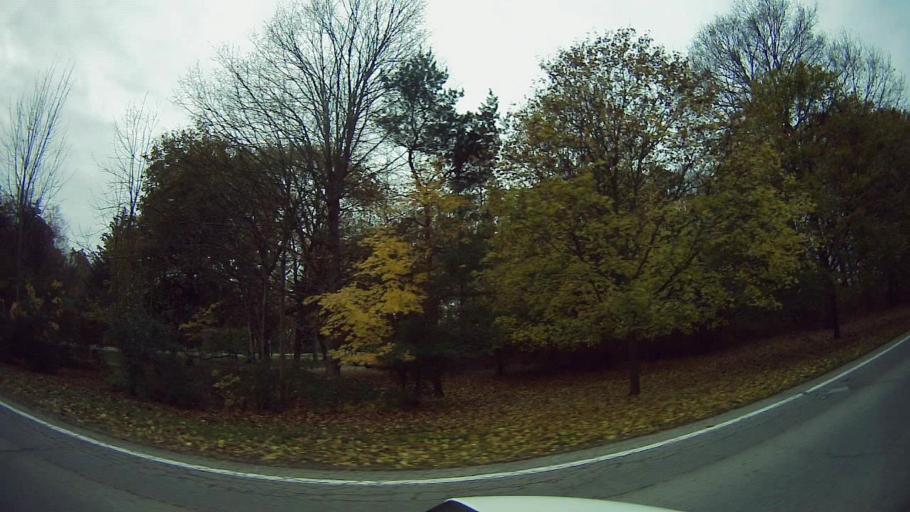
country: US
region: Michigan
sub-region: Oakland County
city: Bingham Farms
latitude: 42.5307
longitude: -83.2577
